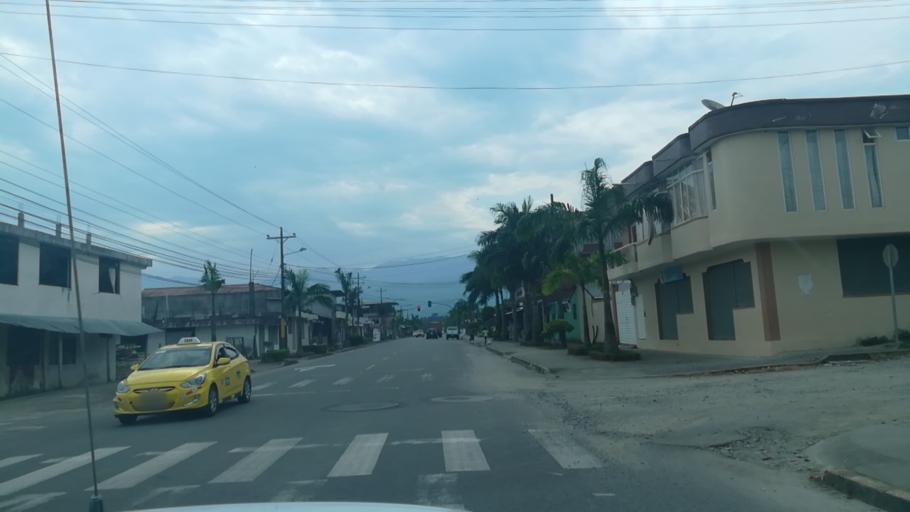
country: EC
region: Napo
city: Tena
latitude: -0.9853
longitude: -77.8182
